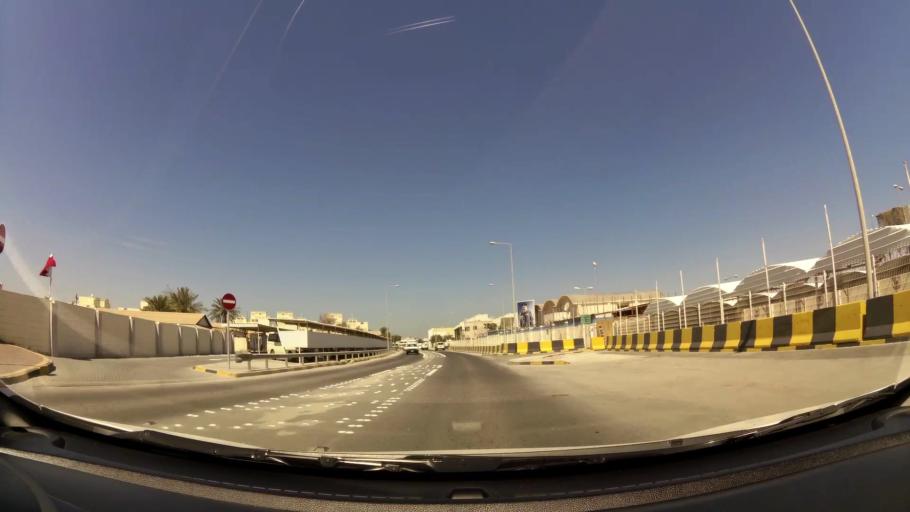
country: BH
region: Muharraq
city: Al Muharraq
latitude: 26.2703
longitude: 50.6150
